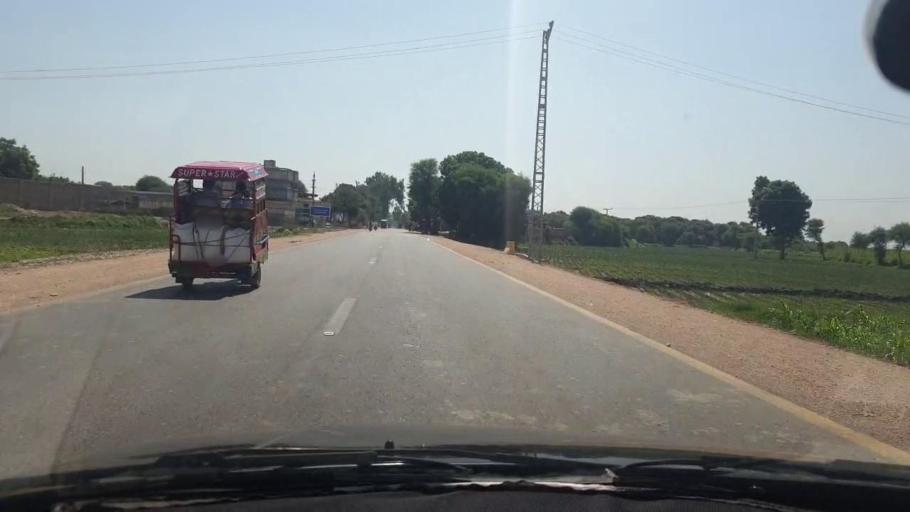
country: PK
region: Sindh
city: Tando Allahyar
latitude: 25.4269
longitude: 68.7505
